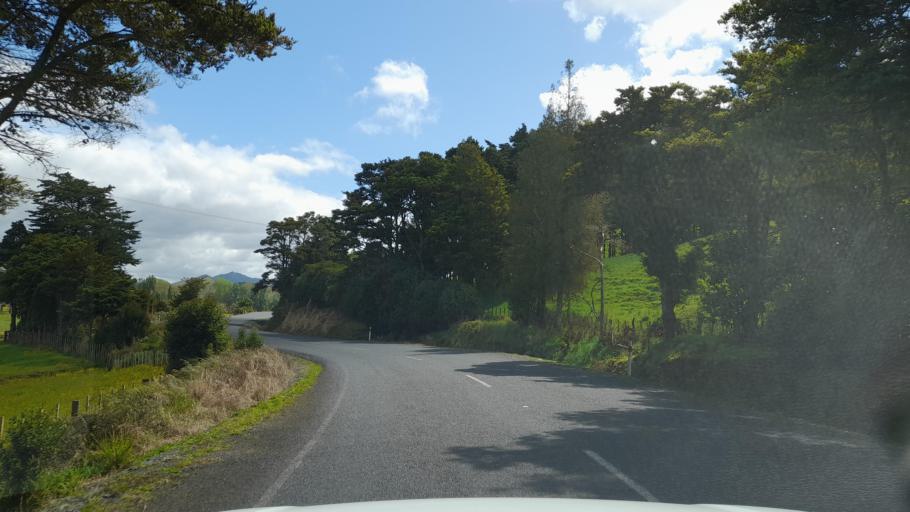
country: NZ
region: Northland
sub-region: Whangarei
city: Maungatapere
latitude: -35.7107
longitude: 174.0553
